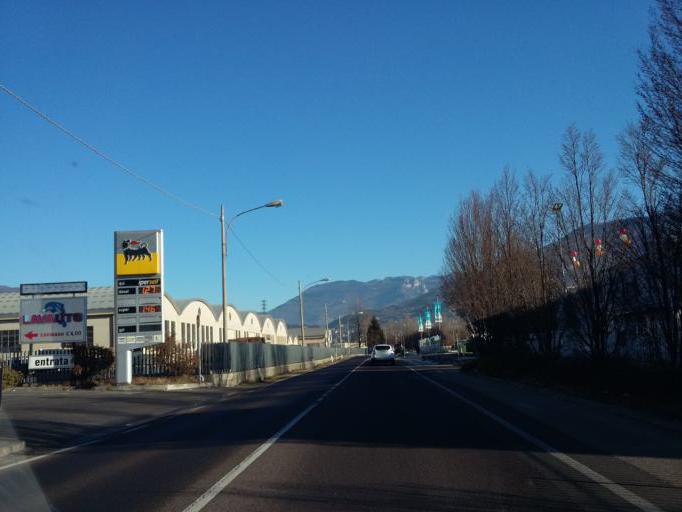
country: IT
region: Trentino-Alto Adige
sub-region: Provincia di Trento
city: Isera
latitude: 45.8710
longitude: 11.0181
